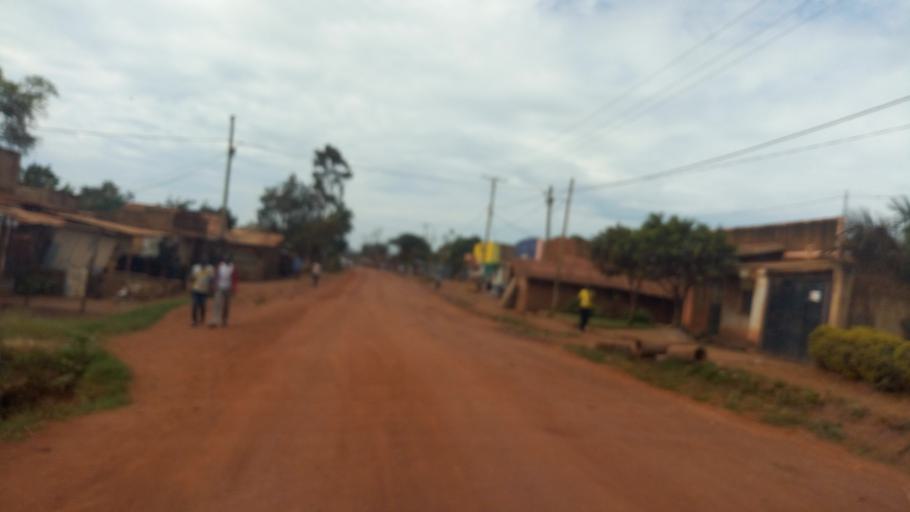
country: UG
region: Central Region
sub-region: Wakiso District
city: Bweyogerere
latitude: 0.3596
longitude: 32.7026
